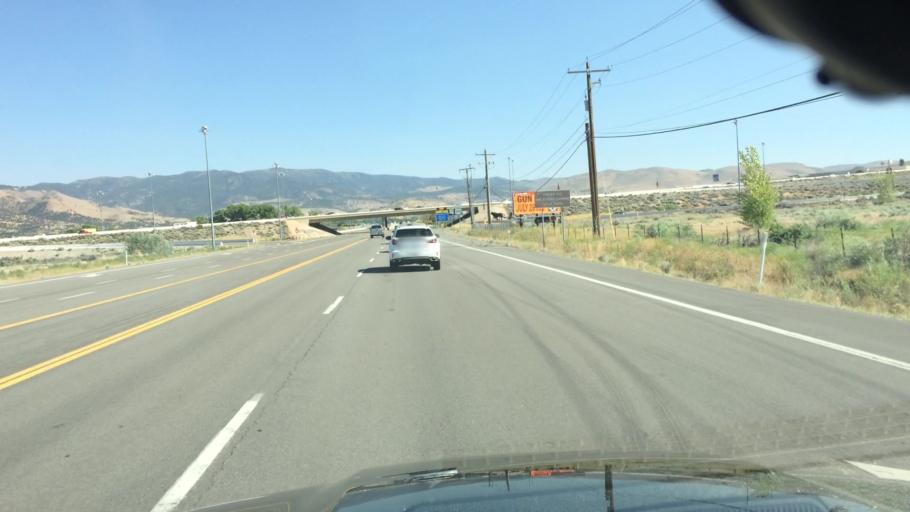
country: US
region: Nevada
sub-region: Washoe County
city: Sparks
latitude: 39.4121
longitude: -119.7524
